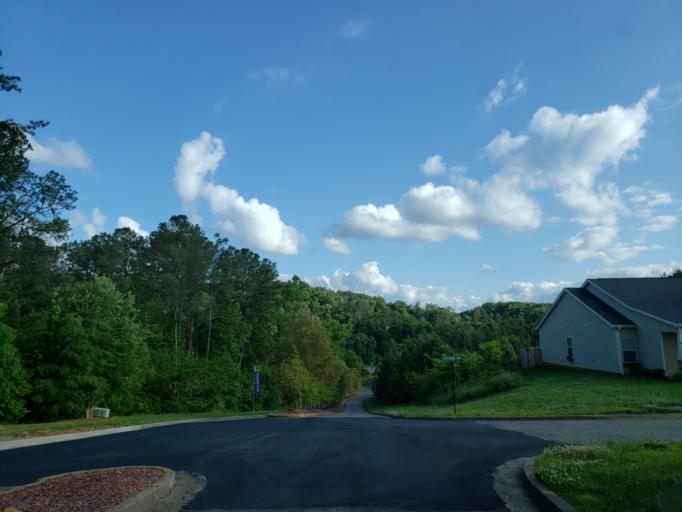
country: US
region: Georgia
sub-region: Bartow County
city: Adairsville
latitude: 34.3865
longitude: -84.8982
